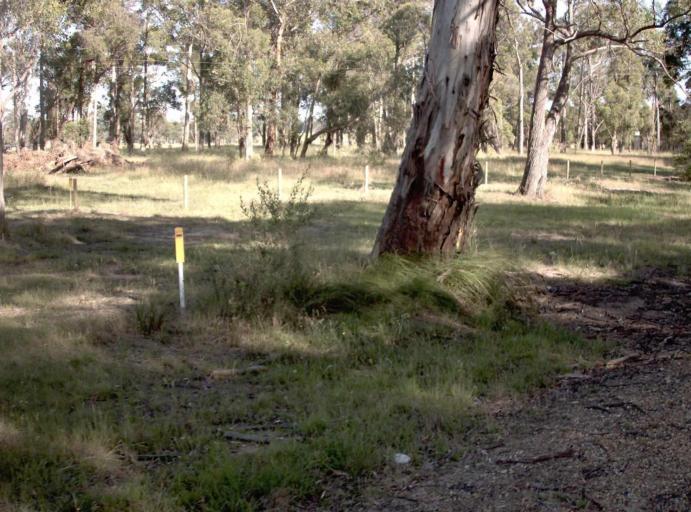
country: AU
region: Victoria
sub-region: East Gippsland
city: Lakes Entrance
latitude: -37.6902
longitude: 148.4688
